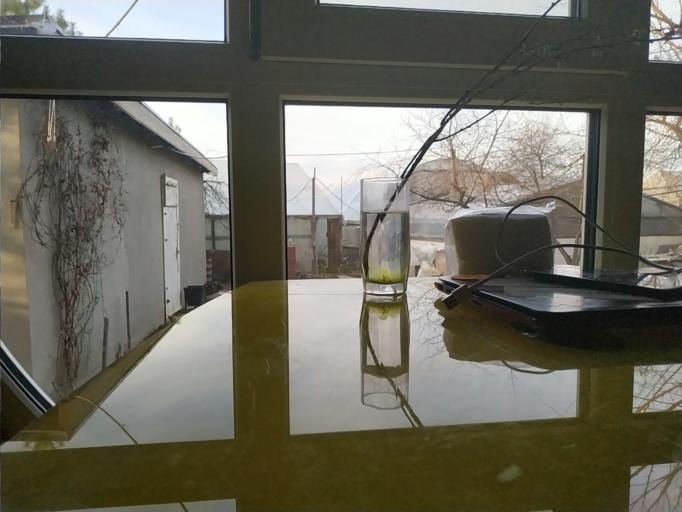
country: RU
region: Republic of Karelia
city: Suoyarvi
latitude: 62.1427
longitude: 32.1444
